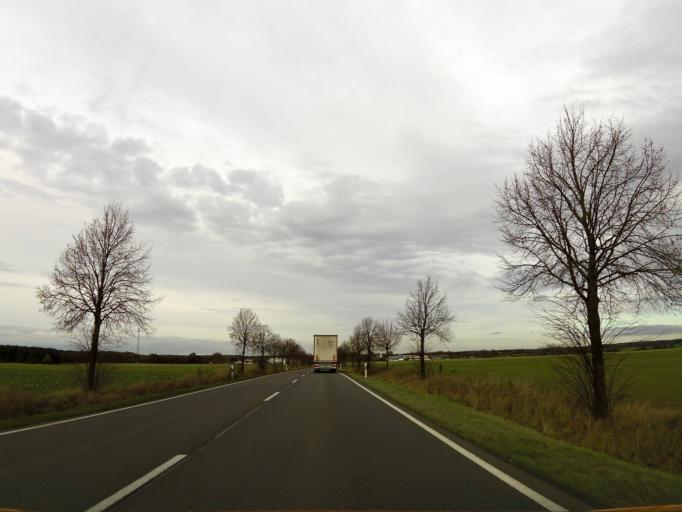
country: DE
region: Saxony-Anhalt
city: Pretzier
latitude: 52.7277
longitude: 11.2468
